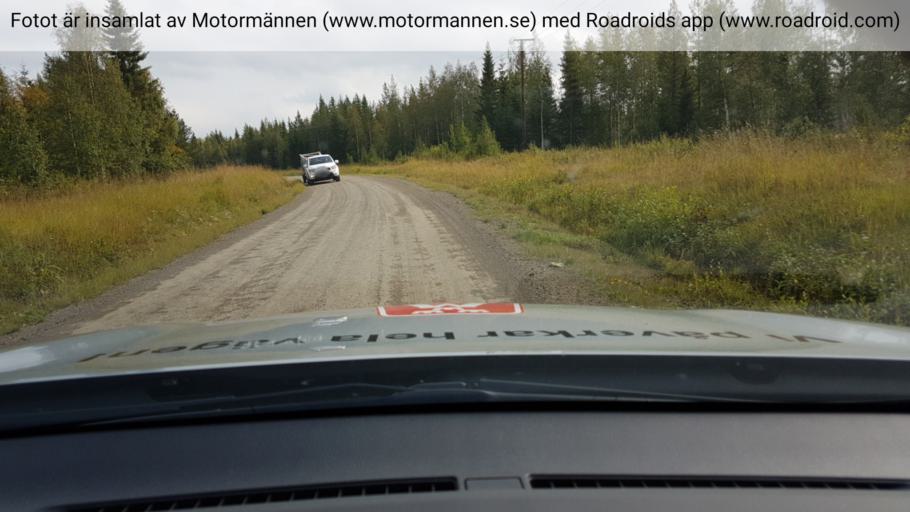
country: SE
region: Jaemtland
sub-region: Stroemsunds Kommun
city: Stroemsund
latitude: 63.7354
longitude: 15.4284
